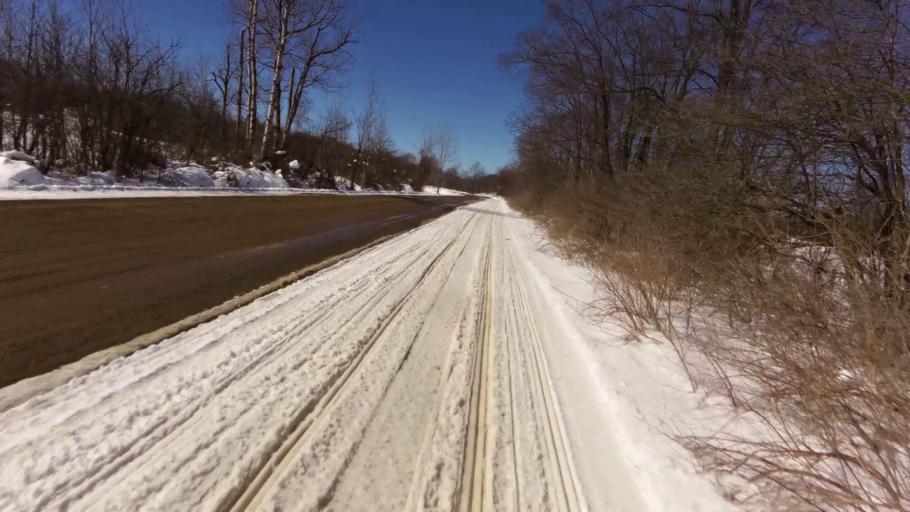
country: US
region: New York
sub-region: Cattaraugus County
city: Delevan
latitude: 42.4353
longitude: -78.4080
